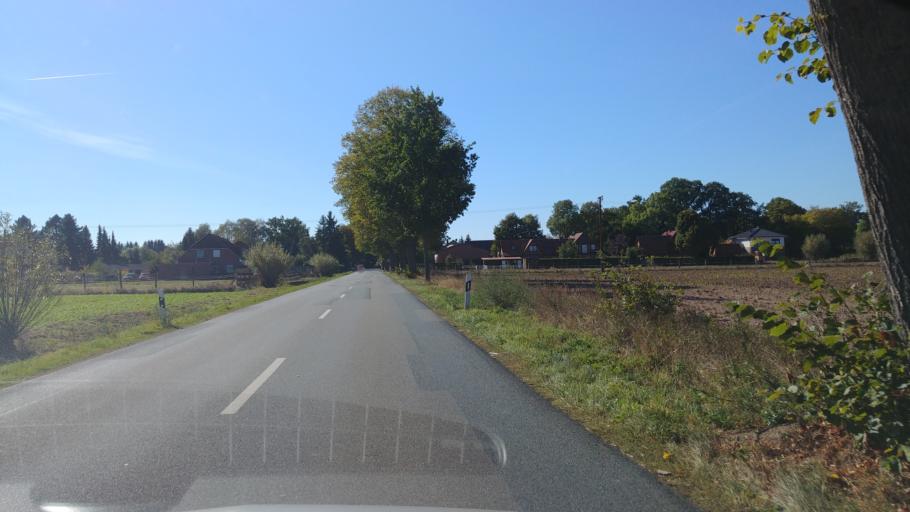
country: DE
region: Lower Saxony
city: Meinersen
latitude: 52.4884
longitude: 10.3431
